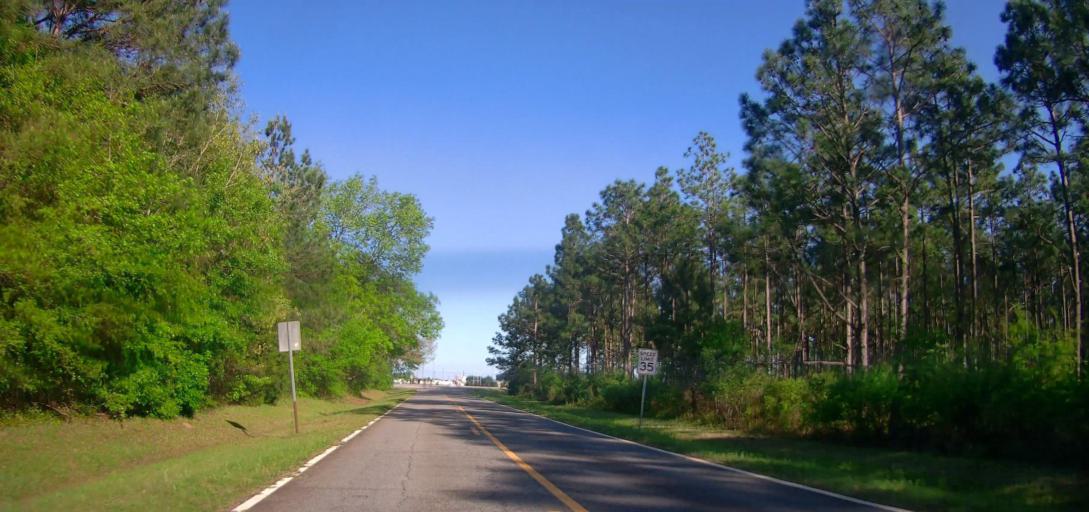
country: US
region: Georgia
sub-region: Houston County
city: Perry
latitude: 32.4679
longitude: -83.7799
